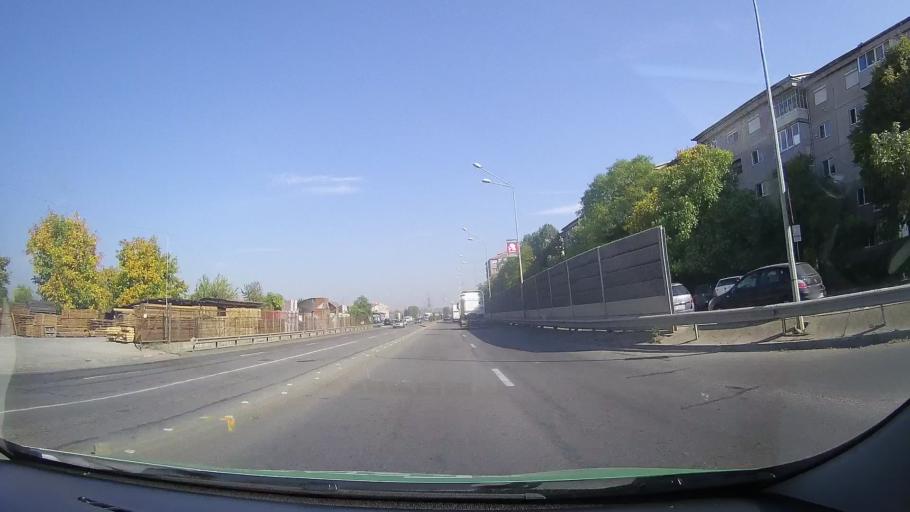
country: RO
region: Bihor
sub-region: Comuna Biharea
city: Oradea
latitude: 47.0666
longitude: 21.8998
